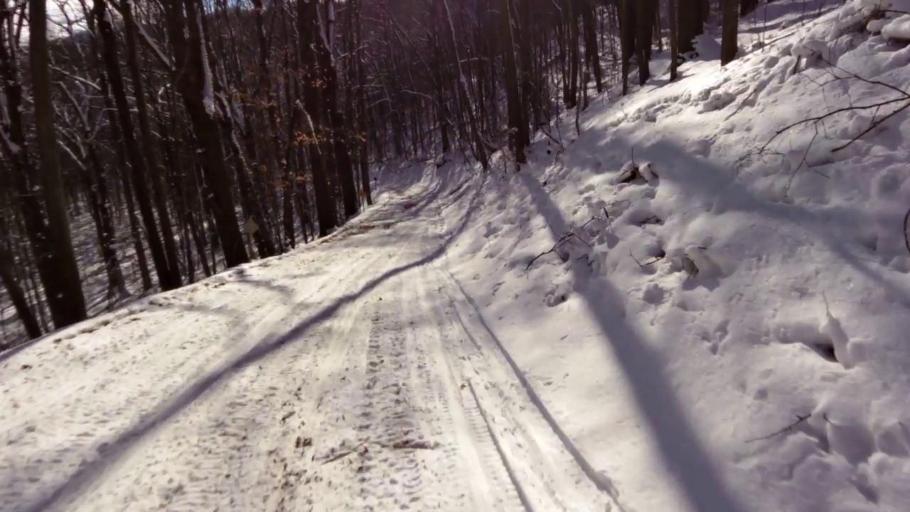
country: US
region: Pennsylvania
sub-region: McKean County
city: Foster Brook
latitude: 42.0679
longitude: -78.6620
